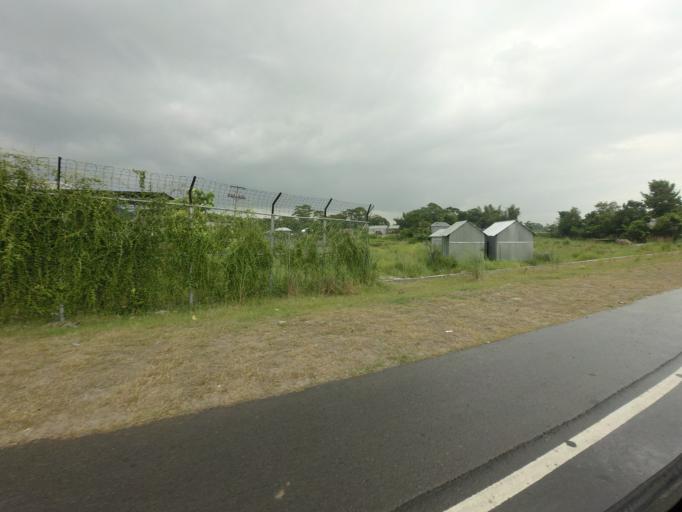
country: BD
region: Dhaka
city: Char Bhadrasan
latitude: 23.3991
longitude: 90.2196
